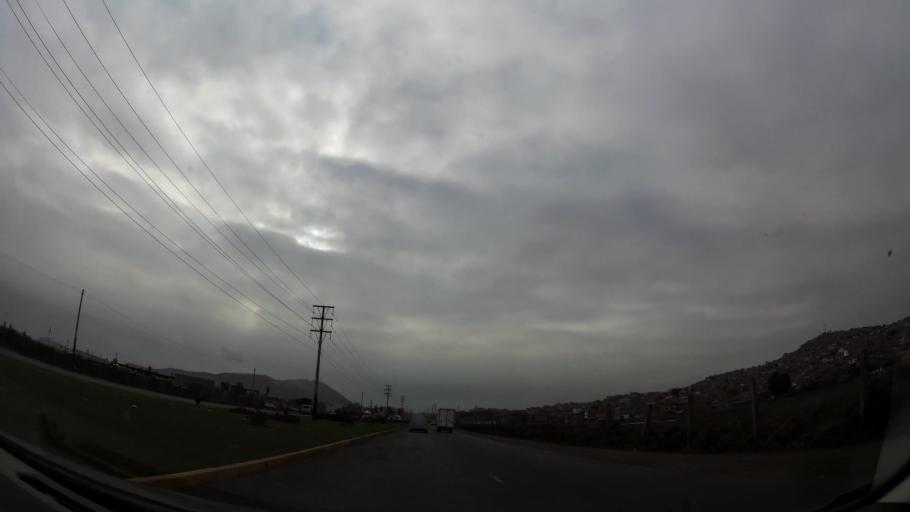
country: PE
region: Lima
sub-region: Lima
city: Surco
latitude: -12.2019
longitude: -76.9946
